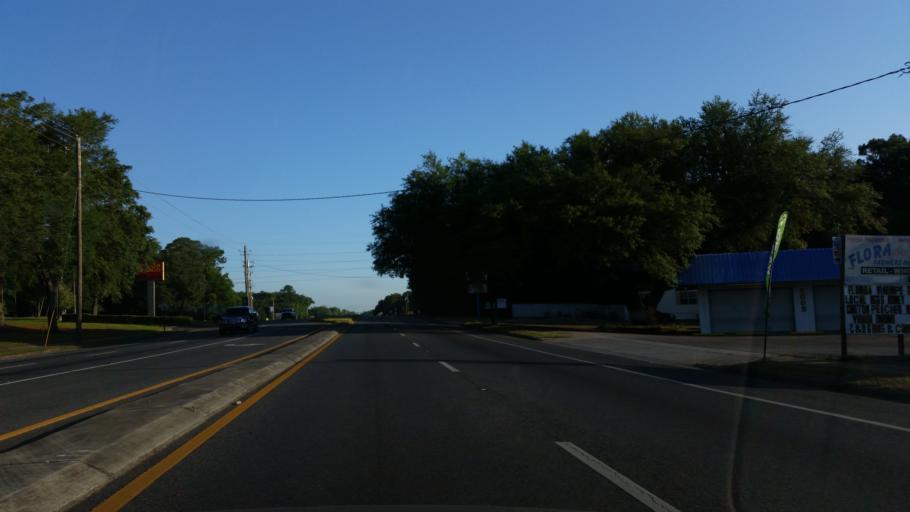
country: US
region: Florida
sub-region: Escambia County
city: Bellview
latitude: 30.4686
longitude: -87.3046
